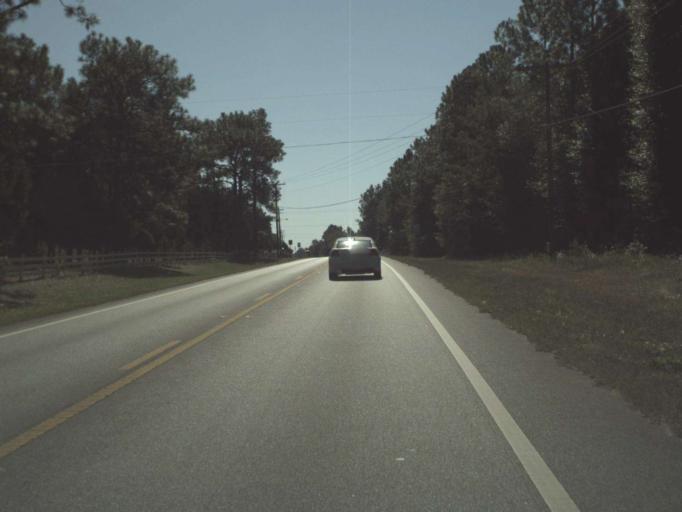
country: US
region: Florida
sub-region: Walton County
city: DeFuniak Springs
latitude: 30.7894
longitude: -86.1208
